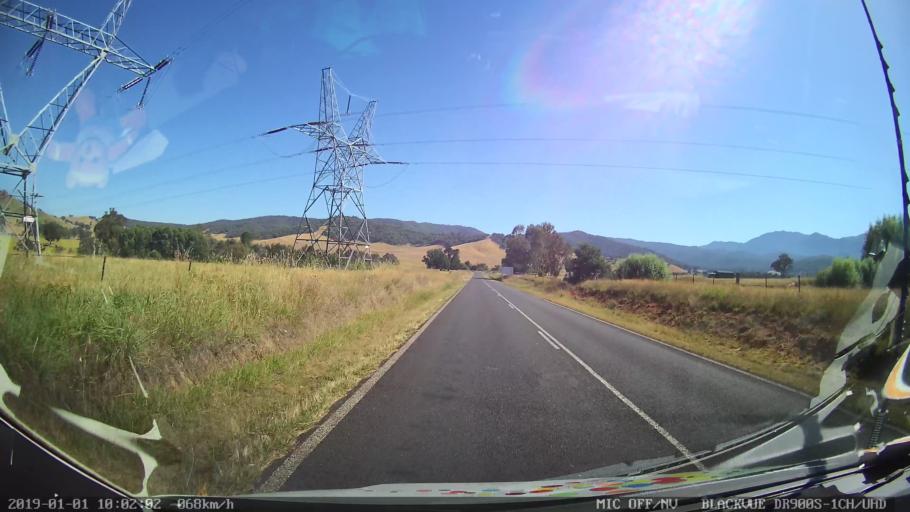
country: AU
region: New South Wales
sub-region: Snowy River
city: Jindabyne
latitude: -36.1853
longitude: 148.1013
